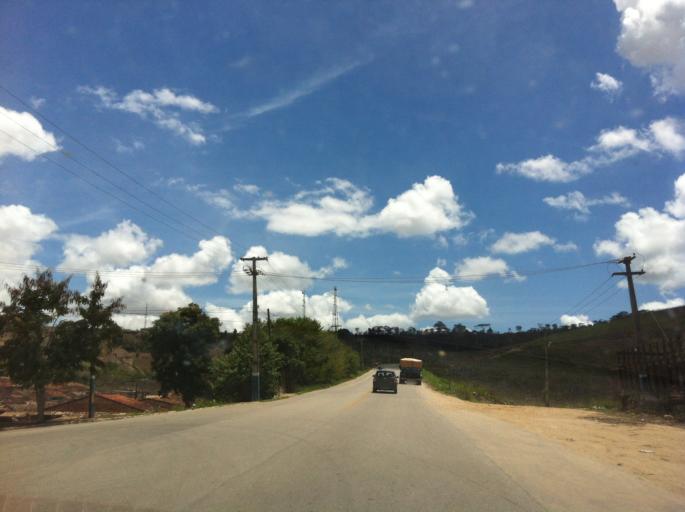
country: BR
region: Alagoas
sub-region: Matriz De Camaragibe
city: Matriz de Camaragibe
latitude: -9.1518
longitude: -35.5251
